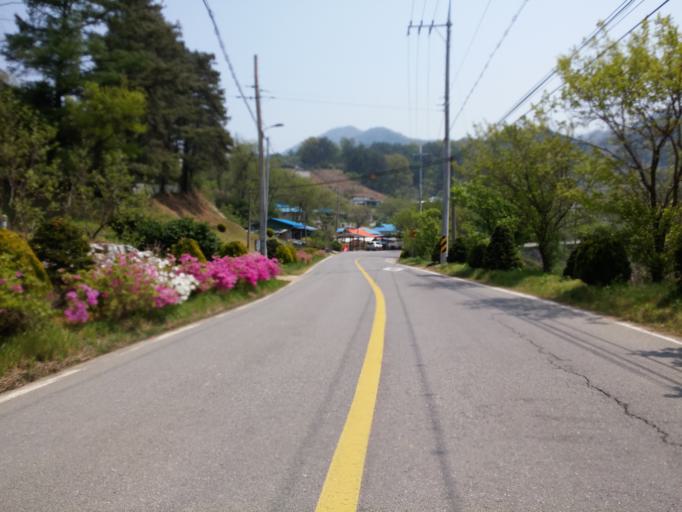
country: KR
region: Chungcheongbuk-do
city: Okcheon
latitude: 36.4477
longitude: 127.5843
